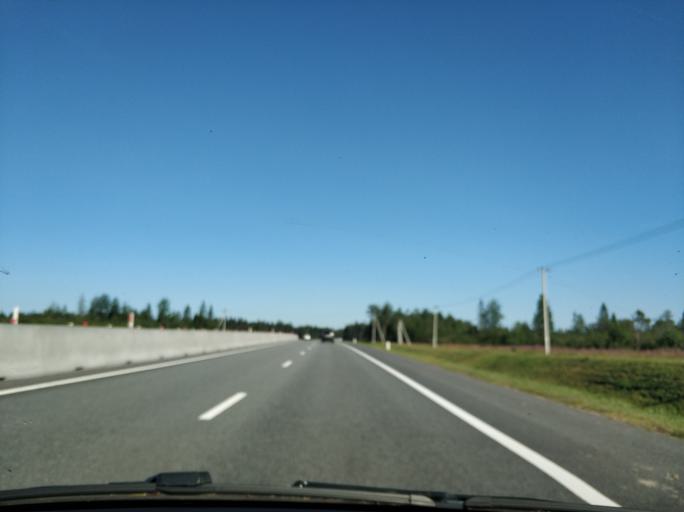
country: RU
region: Leningrad
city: Sosnovo
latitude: 60.5151
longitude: 30.1829
